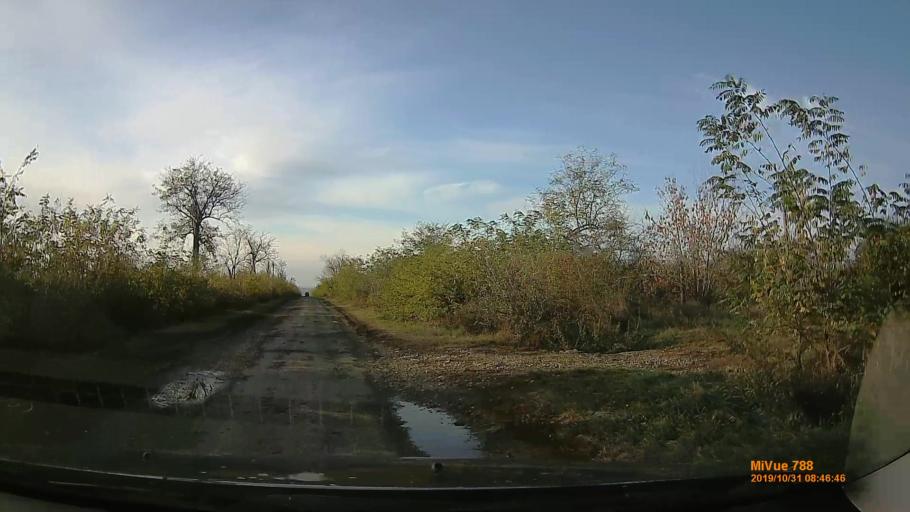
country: HU
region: Pest
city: Albertirsa
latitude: 47.2832
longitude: 19.6101
